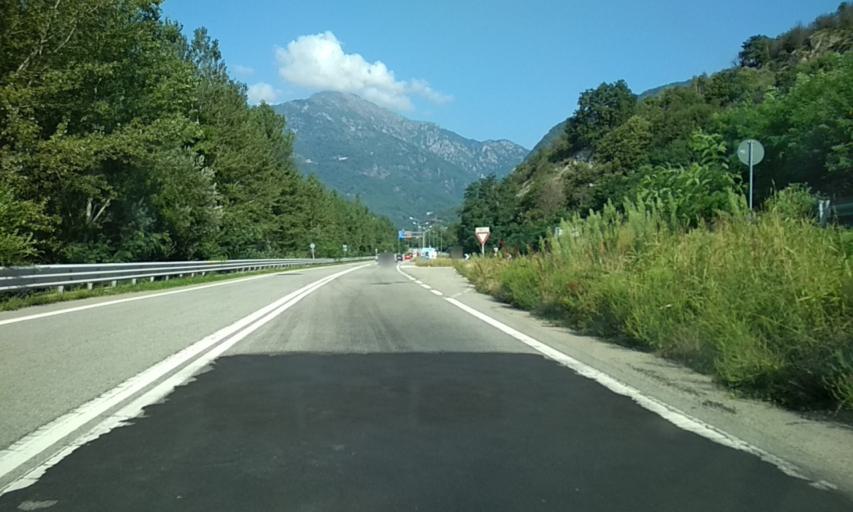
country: IT
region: Piedmont
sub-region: Provincia di Torino
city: Pont-Canavese
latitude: 45.4112
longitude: 7.6216
